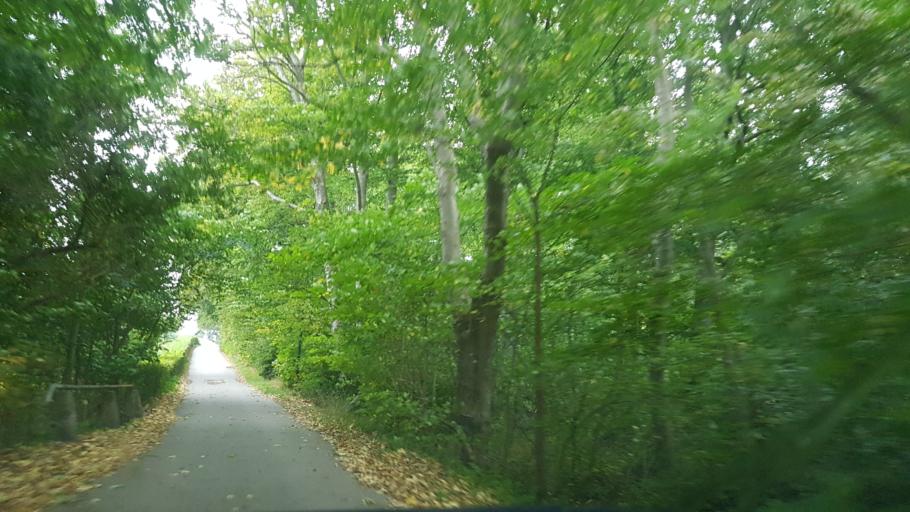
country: DK
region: Capital Region
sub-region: Rudersdal Kommune
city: Trorod
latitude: 55.8416
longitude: 12.5560
